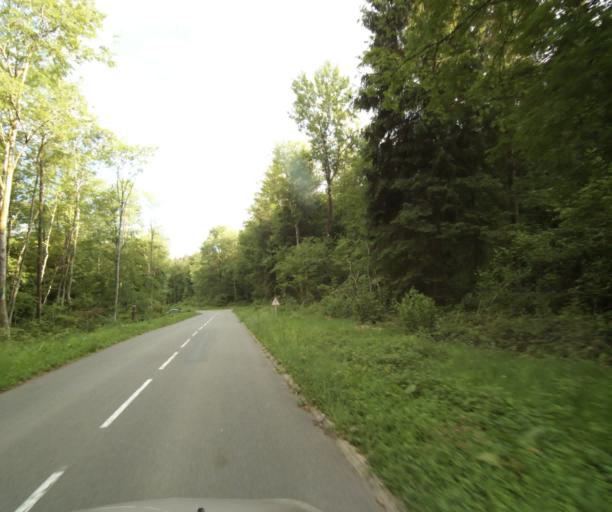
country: FR
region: Champagne-Ardenne
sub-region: Departement des Ardennes
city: Nouzonville
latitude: 49.8237
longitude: 4.7125
